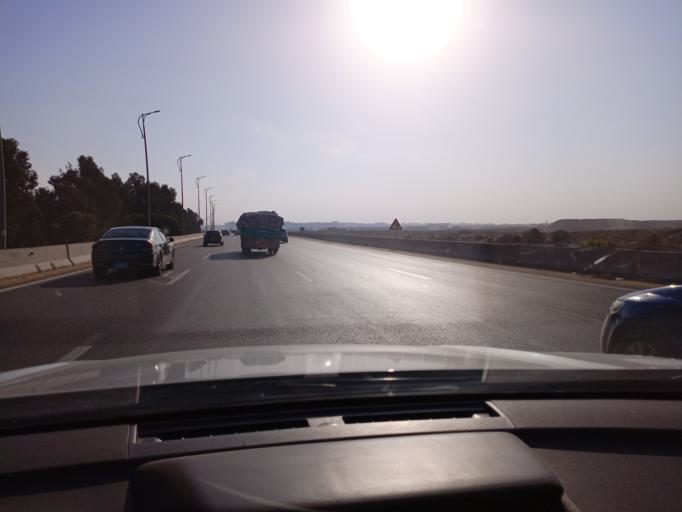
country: EG
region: Muhafazat al Qalyubiyah
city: Al Khankah
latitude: 30.0678
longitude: 31.4236
